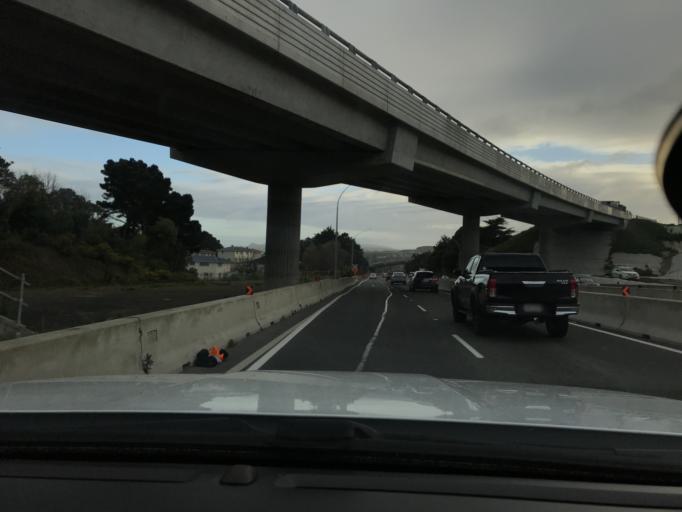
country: NZ
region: Wellington
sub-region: Porirua City
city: Porirua
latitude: -41.1552
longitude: 174.8393
